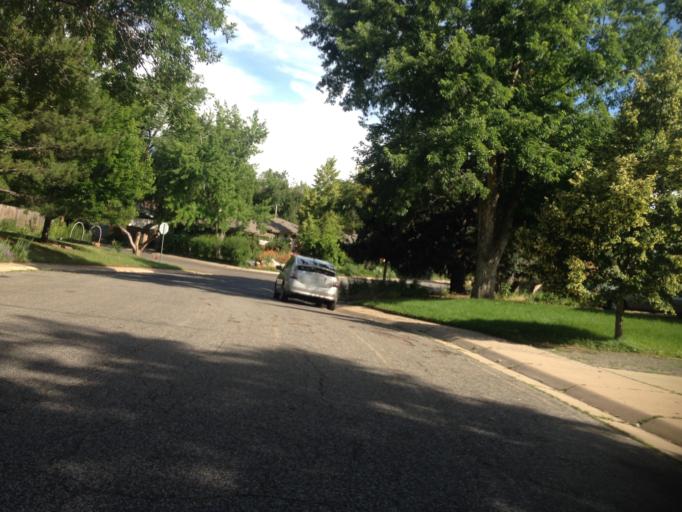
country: US
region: Colorado
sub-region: Boulder County
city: Boulder
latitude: 40.0299
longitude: -105.2752
